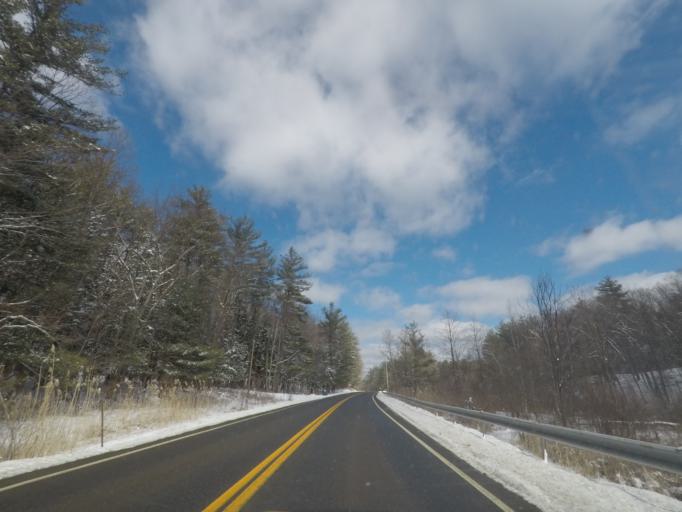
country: US
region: New York
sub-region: Rensselaer County
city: Nassau
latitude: 42.4785
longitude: -73.5223
